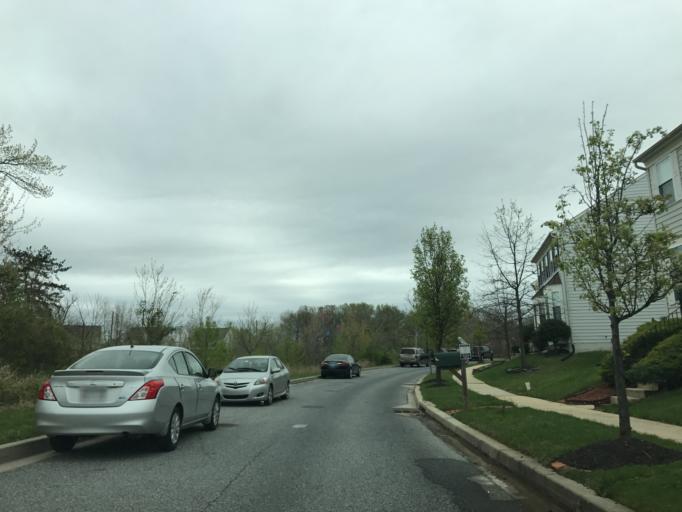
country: US
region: Maryland
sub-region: Baltimore County
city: Middle River
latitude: 39.3278
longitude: -76.4488
